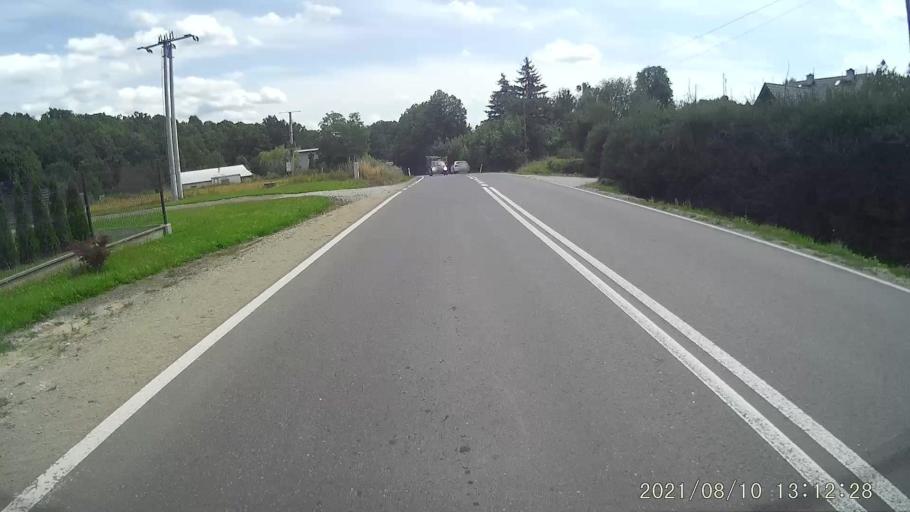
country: PL
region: Lower Silesian Voivodeship
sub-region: Powiat klodzki
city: Bozkow
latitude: 50.5158
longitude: 16.5128
